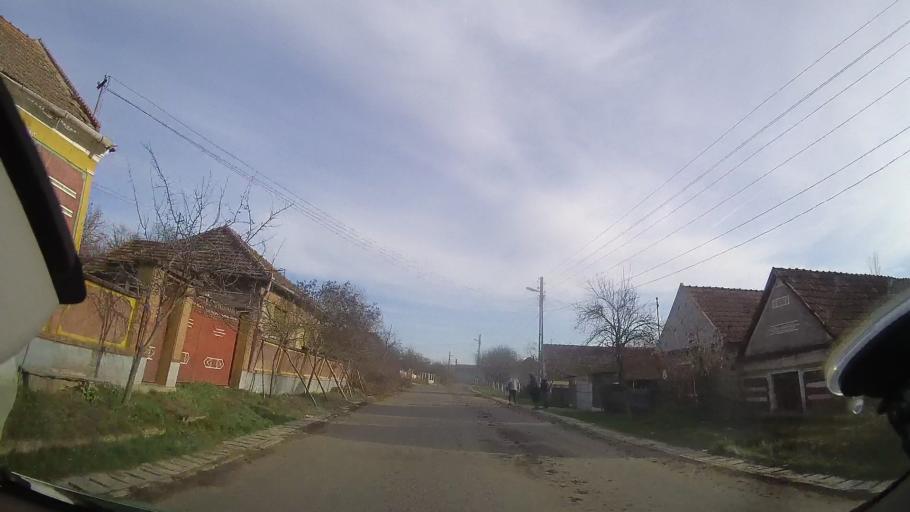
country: RO
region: Bihor
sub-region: Comuna Sarbi
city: Burzuc
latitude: 47.1476
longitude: 22.1791
